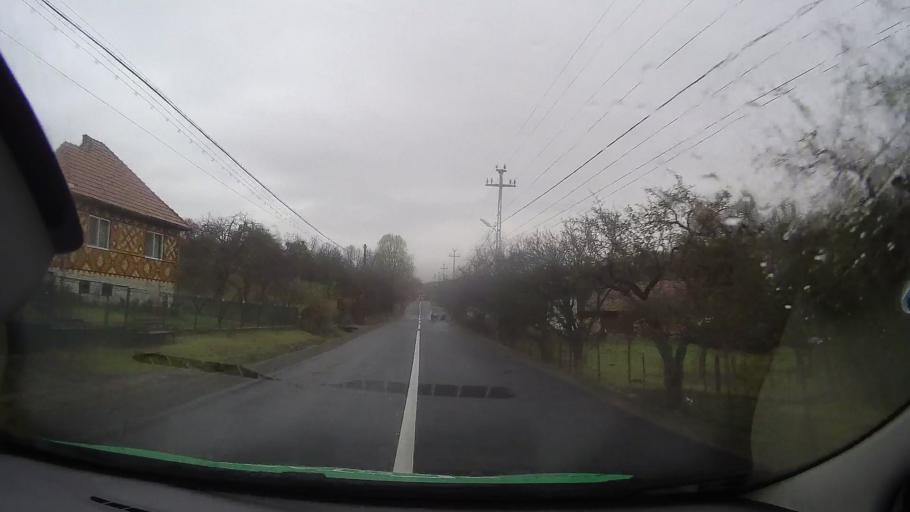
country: RO
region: Mures
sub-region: Comuna Vatava
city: Vatava
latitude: 46.9501
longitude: 24.7623
